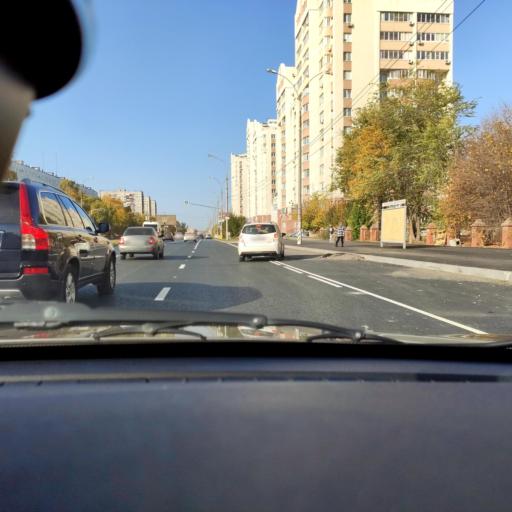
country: RU
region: Samara
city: Tol'yatti
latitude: 53.5139
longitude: 49.2917
